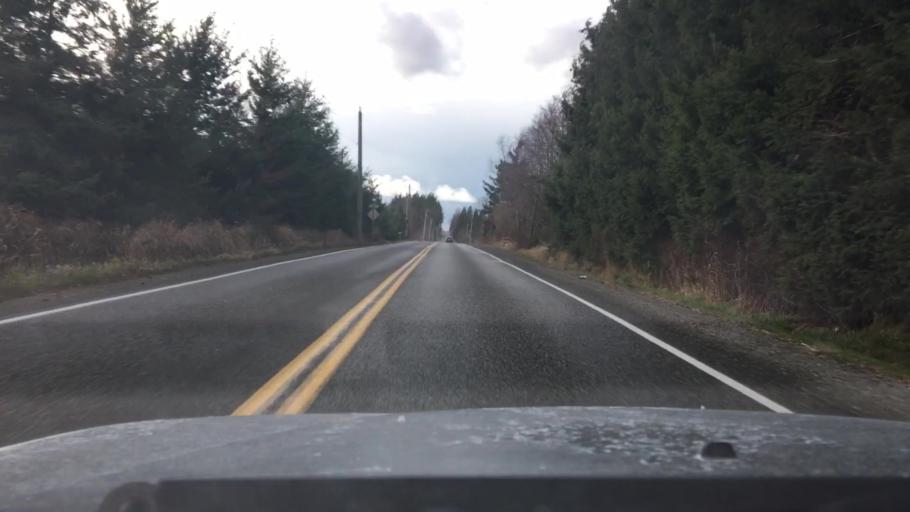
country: US
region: Washington
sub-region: Whatcom County
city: Ferndale
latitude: 48.8483
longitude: -122.6621
